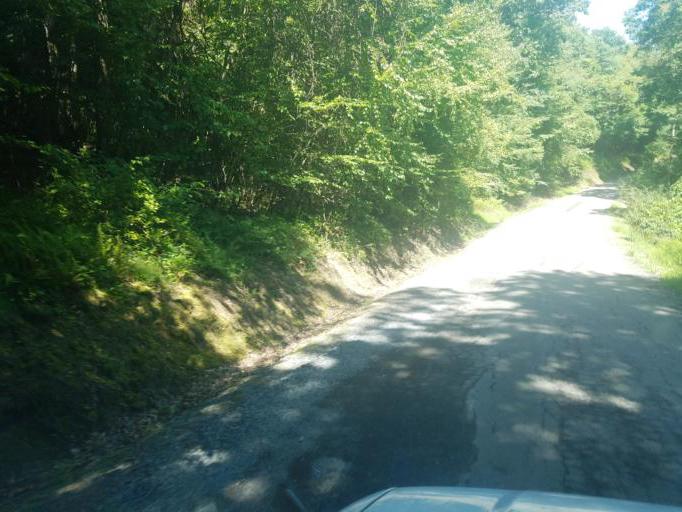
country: US
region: Pennsylvania
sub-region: Clarion County
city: Clarion
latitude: 41.1773
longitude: -79.4312
